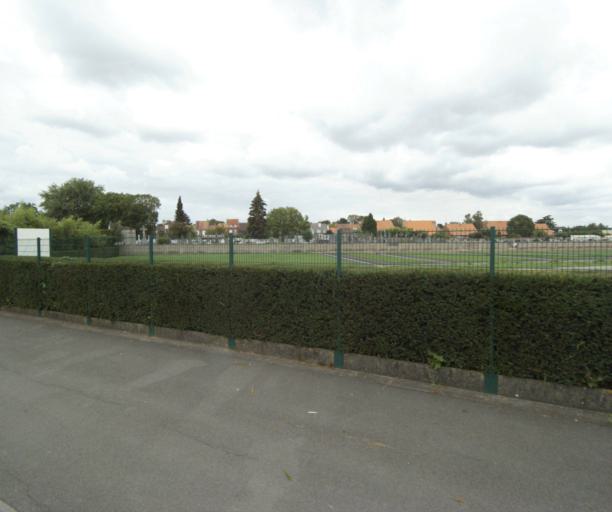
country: FR
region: Nord-Pas-de-Calais
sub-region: Departement du Nord
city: Villeneuve-d'Ascq
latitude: 50.6189
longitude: 3.1677
